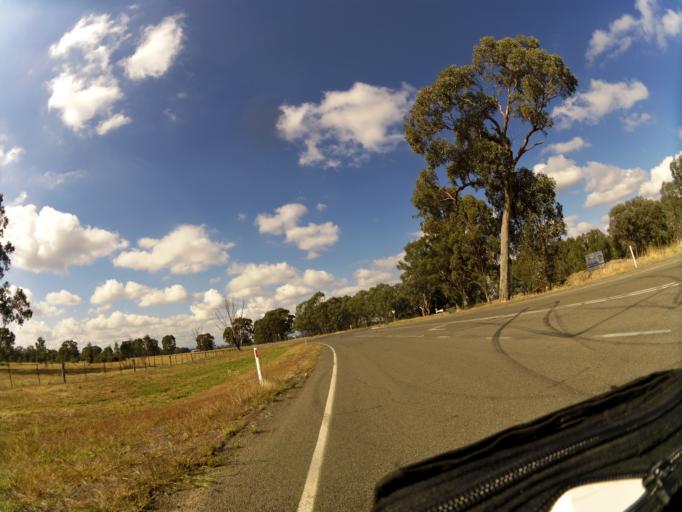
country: AU
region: Victoria
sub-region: Benalla
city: Benalla
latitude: -36.5772
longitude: 145.9911
